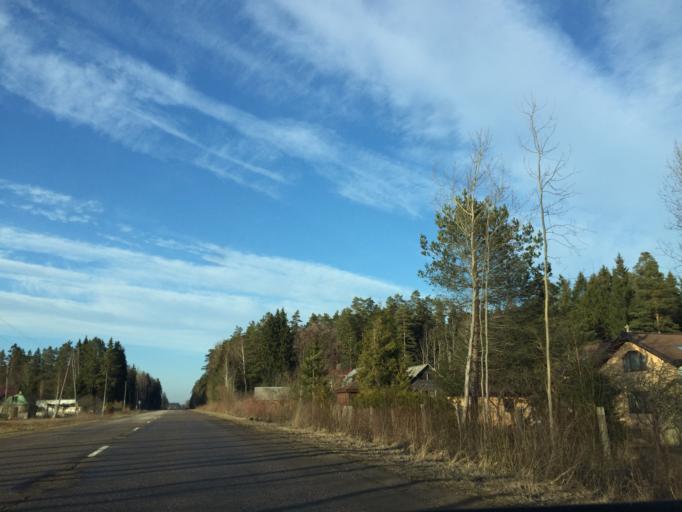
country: LV
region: Lecava
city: Iecava
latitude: 56.7173
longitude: 24.1117
